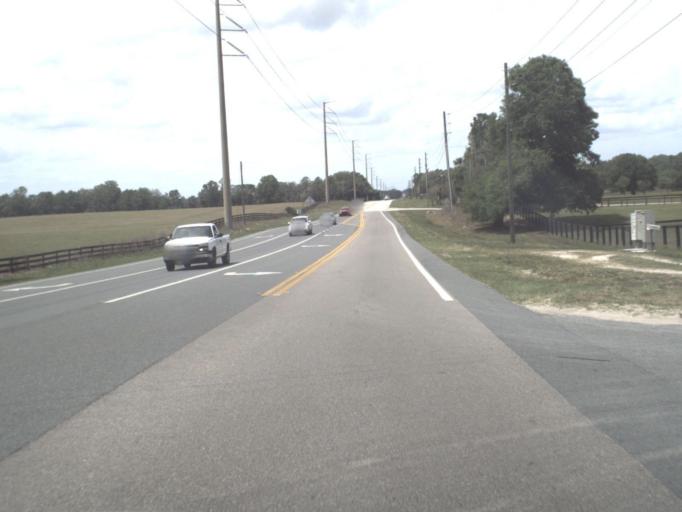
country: US
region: Florida
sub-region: Lake County
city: Mount Plymouth
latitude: 28.8512
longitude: -81.5768
